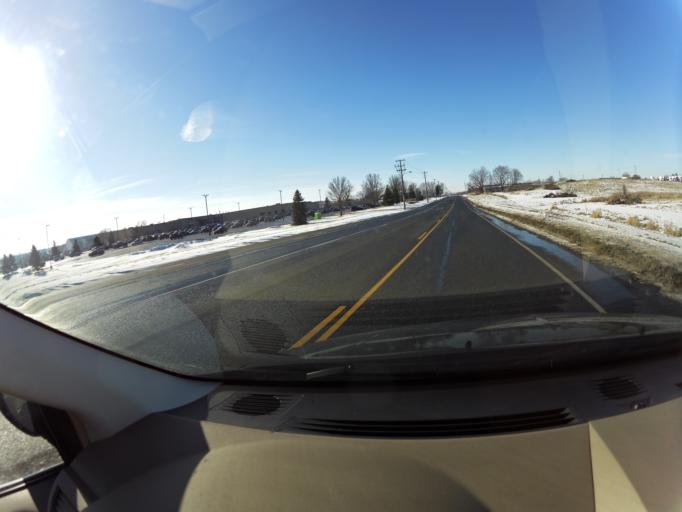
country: US
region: Minnesota
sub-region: Olmsted County
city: Rochester
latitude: 44.0434
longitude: -92.5054
